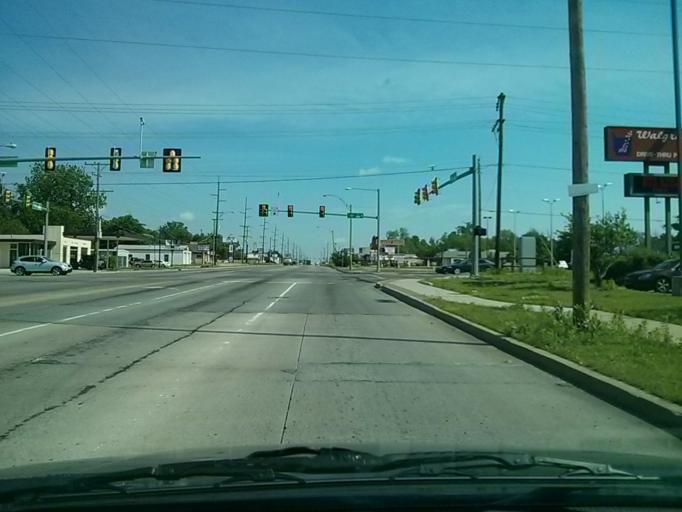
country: US
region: Oklahoma
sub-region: Tulsa County
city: Turley
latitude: 36.2200
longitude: -95.9754
